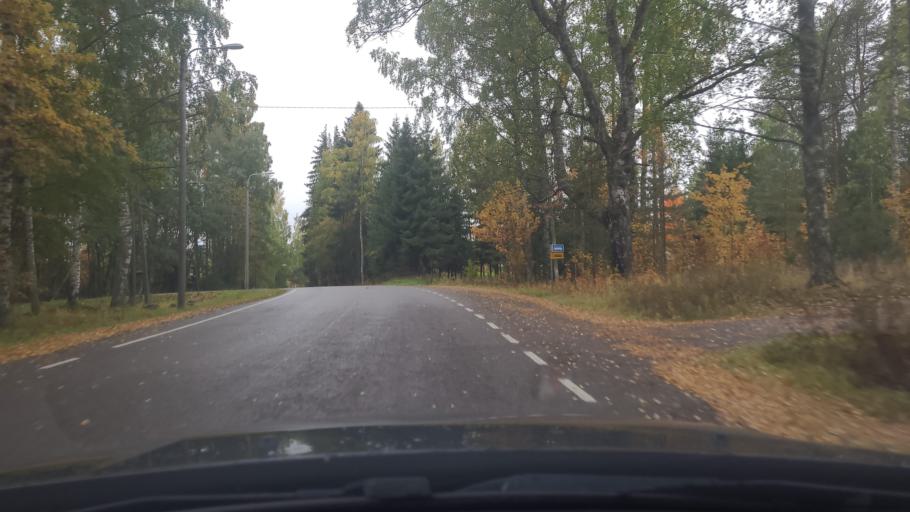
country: FI
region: Northern Savo
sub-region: Varkaus
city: Varkaus
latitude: 62.3126
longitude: 27.9965
